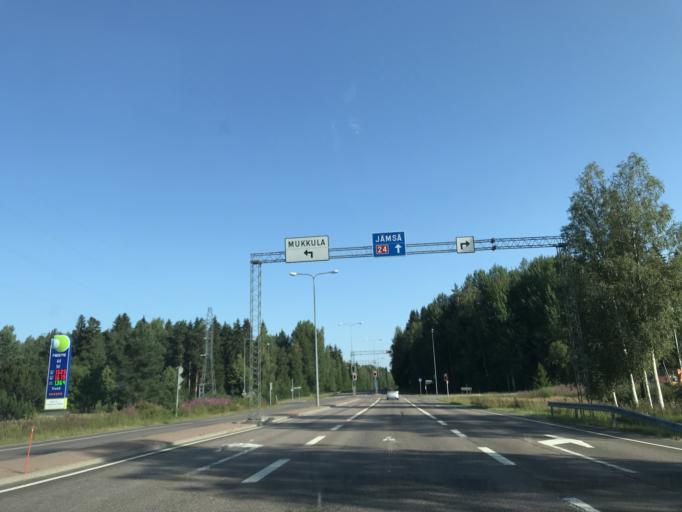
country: FI
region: Paijanne Tavastia
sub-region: Lahti
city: Lahti
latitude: 61.0120
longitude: 25.6815
